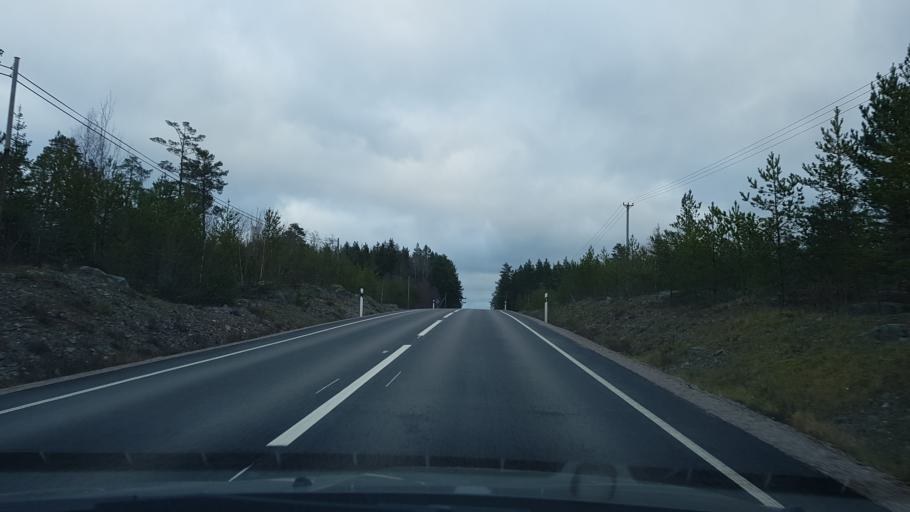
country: SE
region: Stockholm
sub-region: Norrtalje Kommun
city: Nykvarn
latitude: 59.9948
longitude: 18.2870
